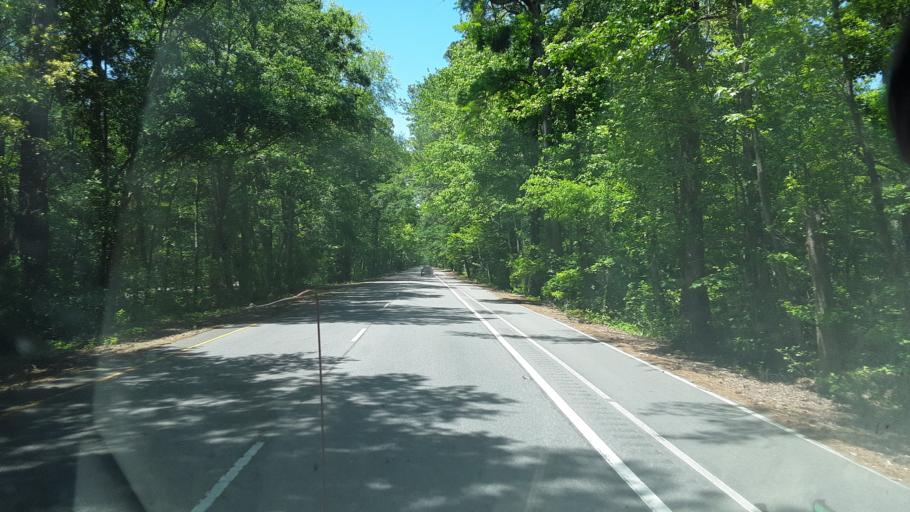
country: US
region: Virginia
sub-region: City of Virginia Beach
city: Virginia Beach
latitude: 36.9136
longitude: -76.0097
